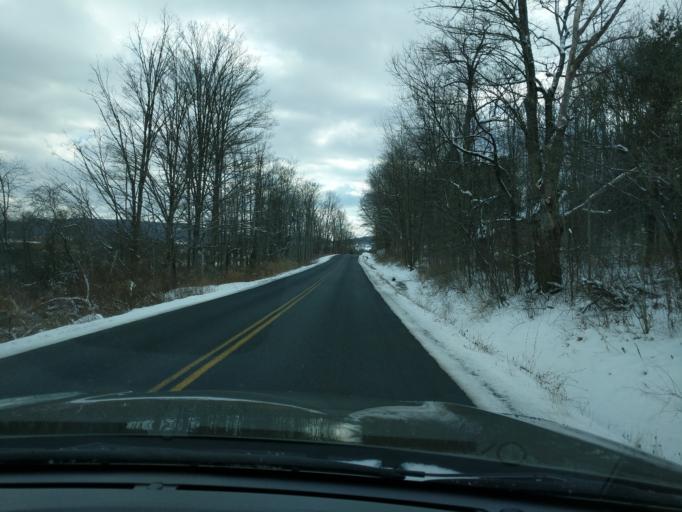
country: US
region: New York
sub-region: Tompkins County
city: East Ithaca
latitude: 42.4012
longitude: -76.3784
